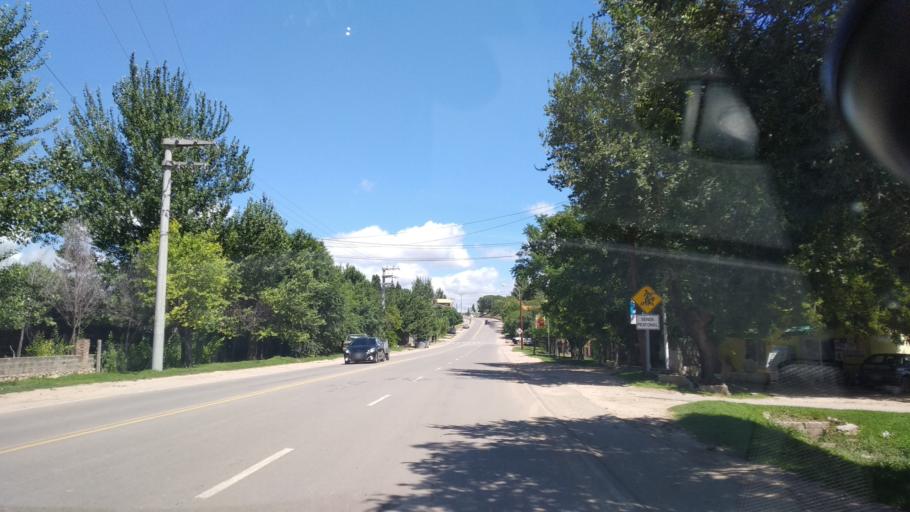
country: AR
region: Cordoba
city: Villa Cura Brochero
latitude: -31.7052
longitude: -65.0238
